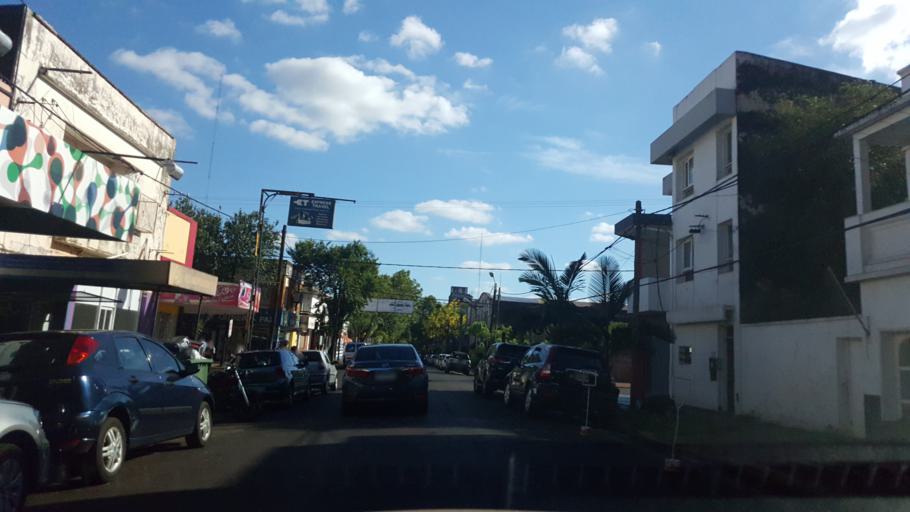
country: AR
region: Misiones
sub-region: Departamento de Capital
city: Posadas
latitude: -27.3694
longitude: -55.8940
